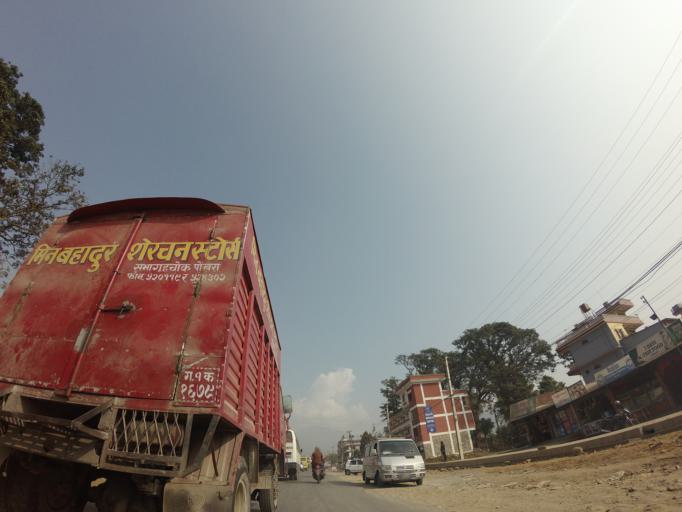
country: NP
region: Western Region
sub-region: Gandaki Zone
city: Pokhara
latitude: 28.2234
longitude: 83.9791
